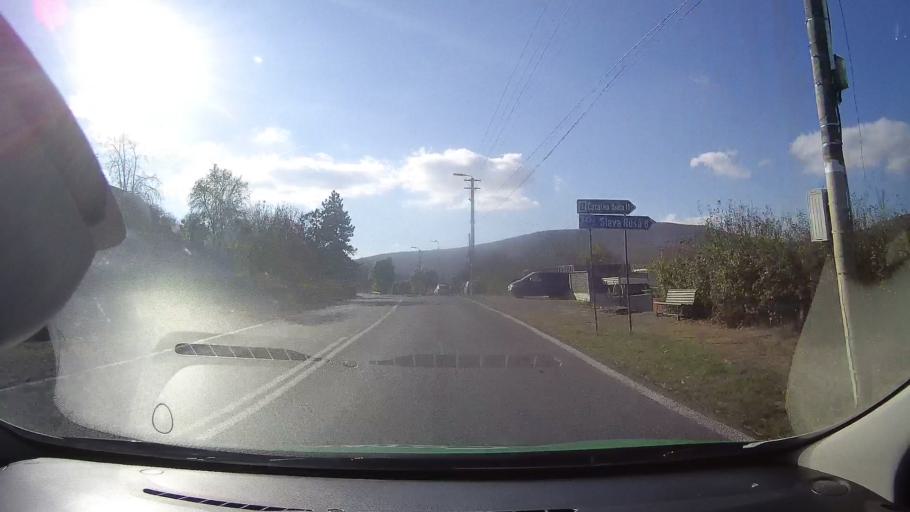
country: RO
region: Tulcea
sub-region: Oras Babadag
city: Babadag
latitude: 44.8794
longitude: 28.6924
